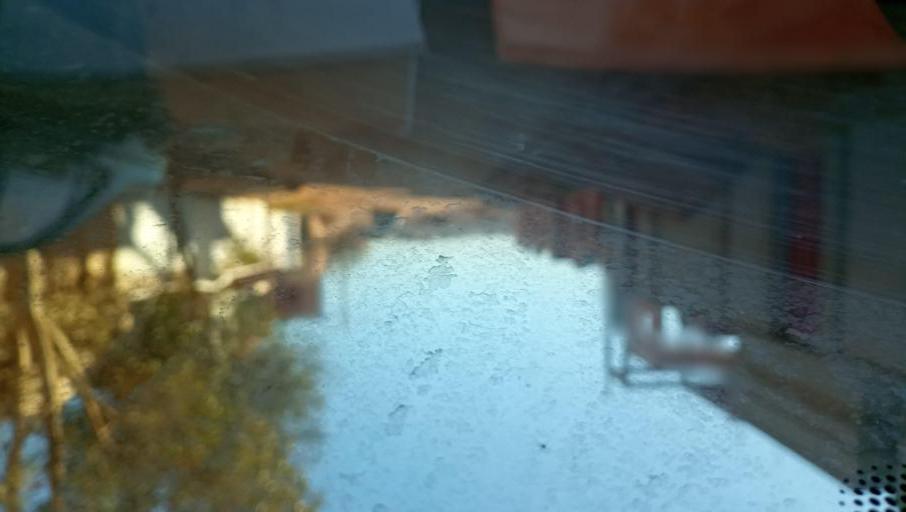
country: TN
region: Tataouine
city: Tataouine
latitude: 32.9869
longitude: 10.4597
